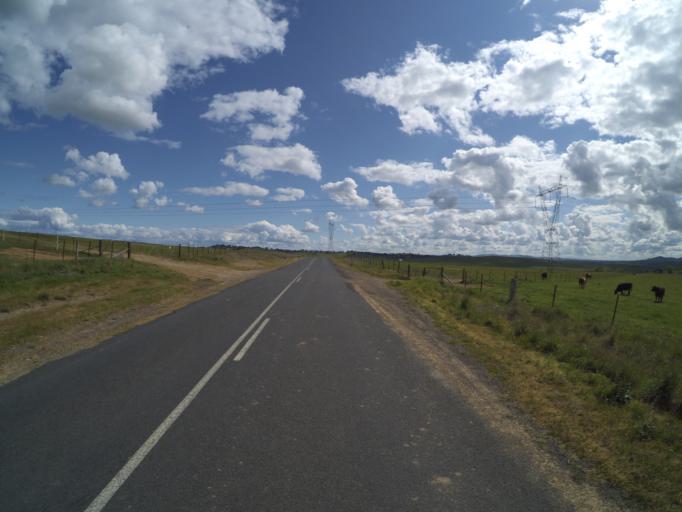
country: AU
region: New South Wales
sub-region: Yass Valley
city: Yass
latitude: -34.8738
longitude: 148.9088
